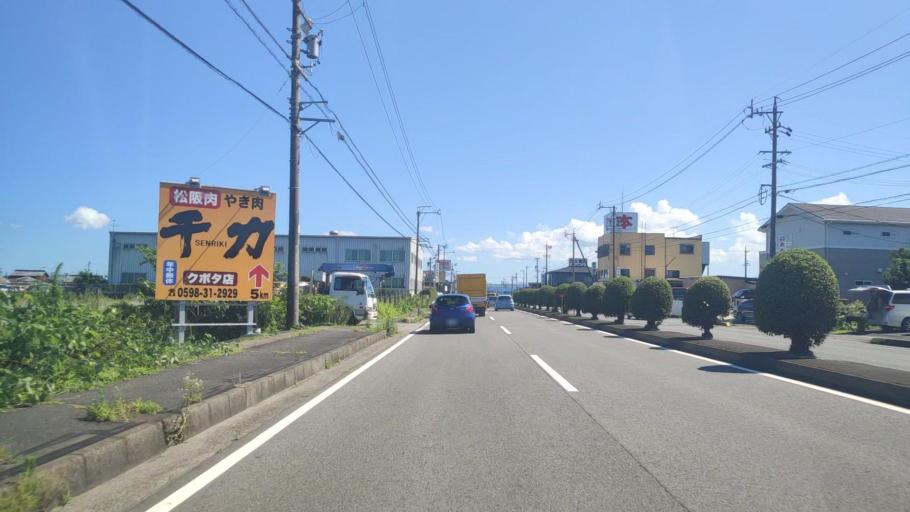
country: JP
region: Mie
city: Hisai-motomachi
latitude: 34.6294
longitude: 136.5168
